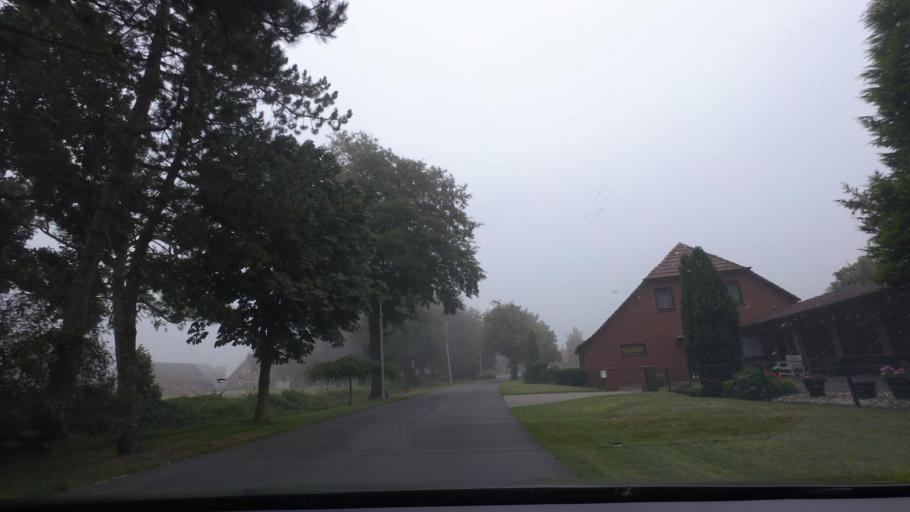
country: DE
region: Lower Saxony
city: Hatten
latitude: 53.1183
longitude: 8.3500
